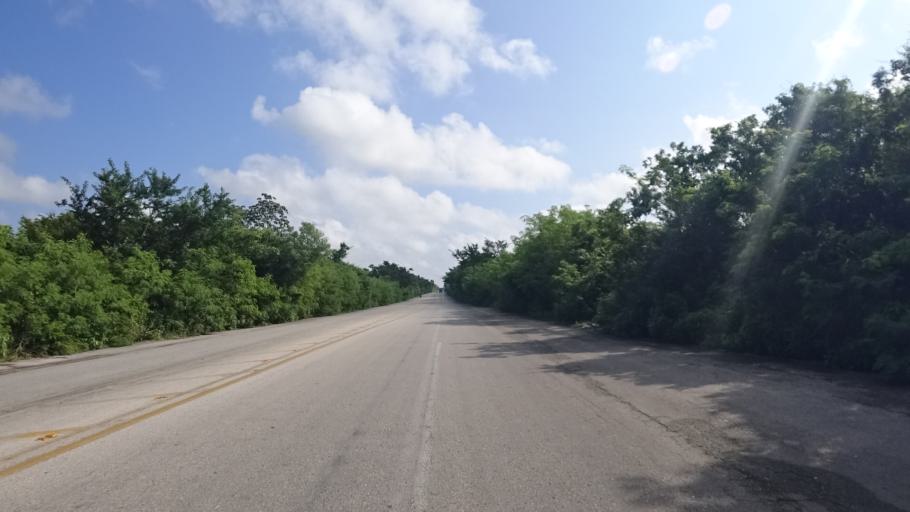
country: MX
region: Yucatan
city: Valladolid
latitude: 20.7038
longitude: -88.2401
